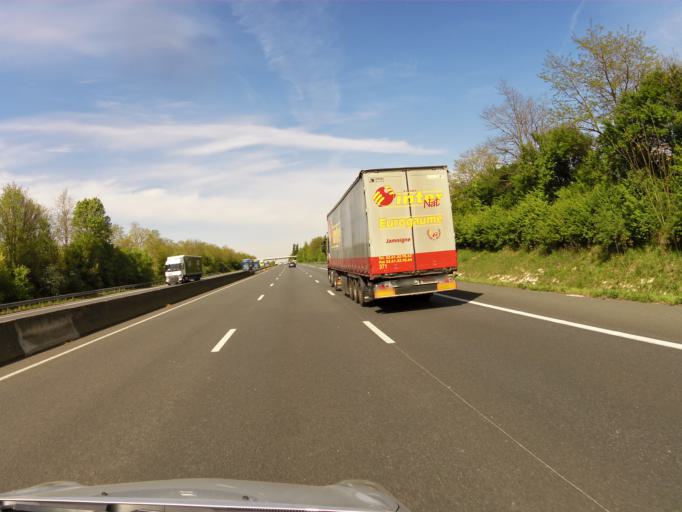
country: FR
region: Centre
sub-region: Departement d'Eure-et-Loir
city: Janville
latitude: 48.1737
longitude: 1.8541
